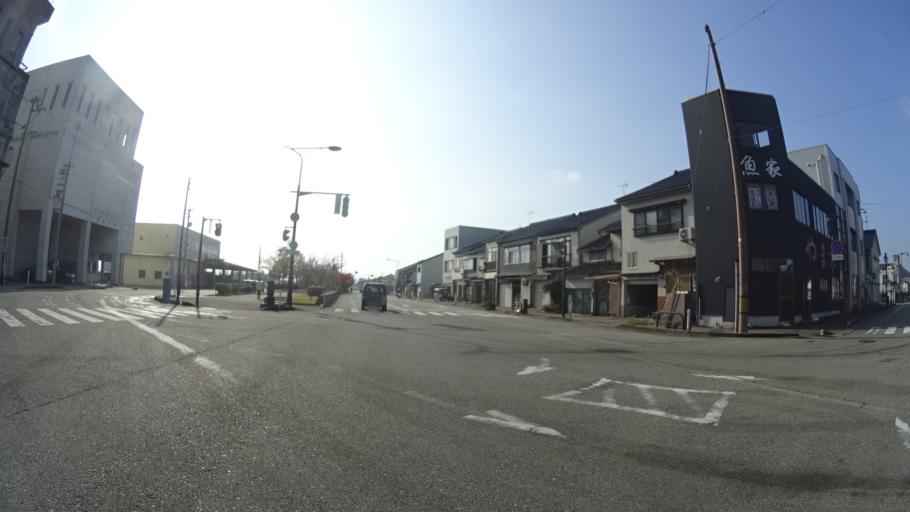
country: JP
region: Toyama
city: Himi
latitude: 36.8601
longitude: 136.9885
